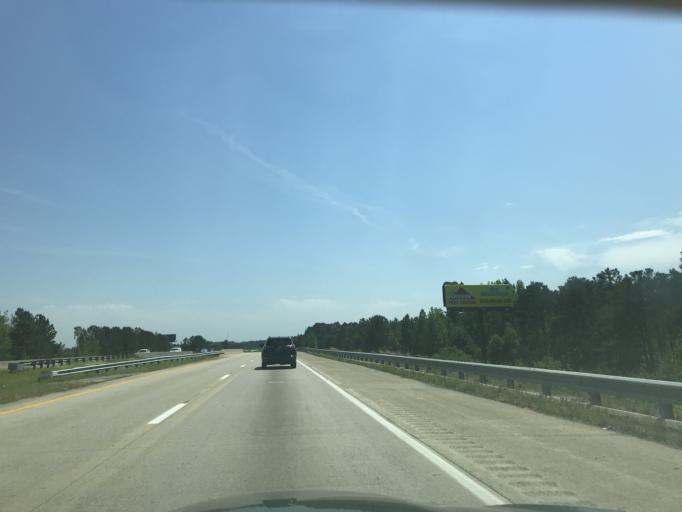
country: US
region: North Carolina
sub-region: Johnston County
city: Benson
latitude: 35.4061
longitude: -78.5239
